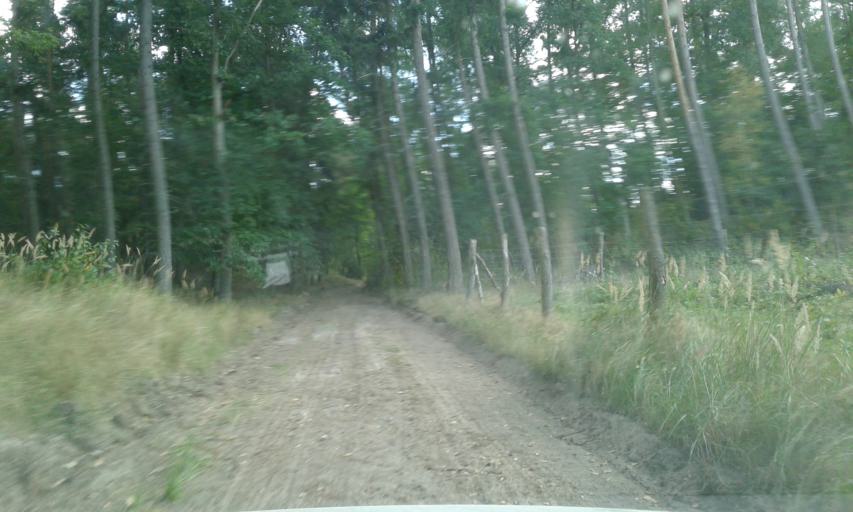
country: PL
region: West Pomeranian Voivodeship
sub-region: Powiat stargardzki
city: Dolice
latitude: 53.2346
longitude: 15.2435
